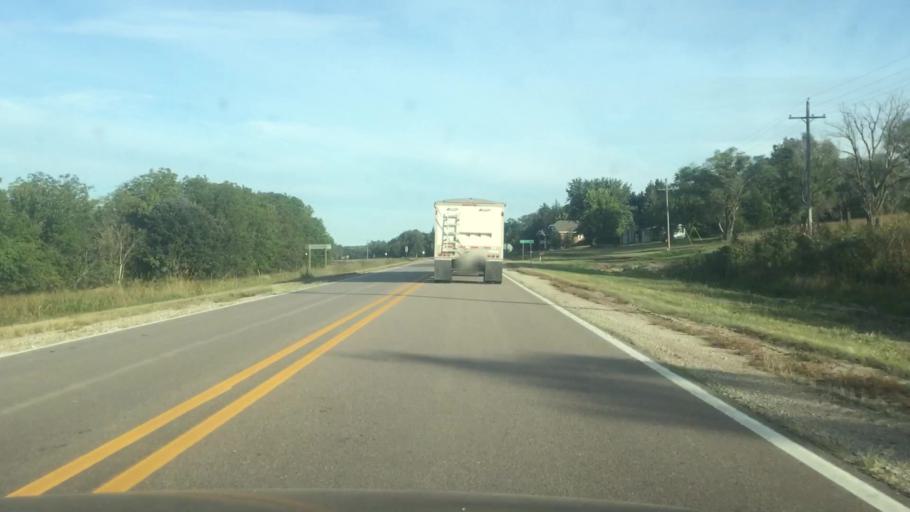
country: US
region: Nebraska
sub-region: Jefferson County
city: Fairbury
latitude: 40.0466
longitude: -97.0246
